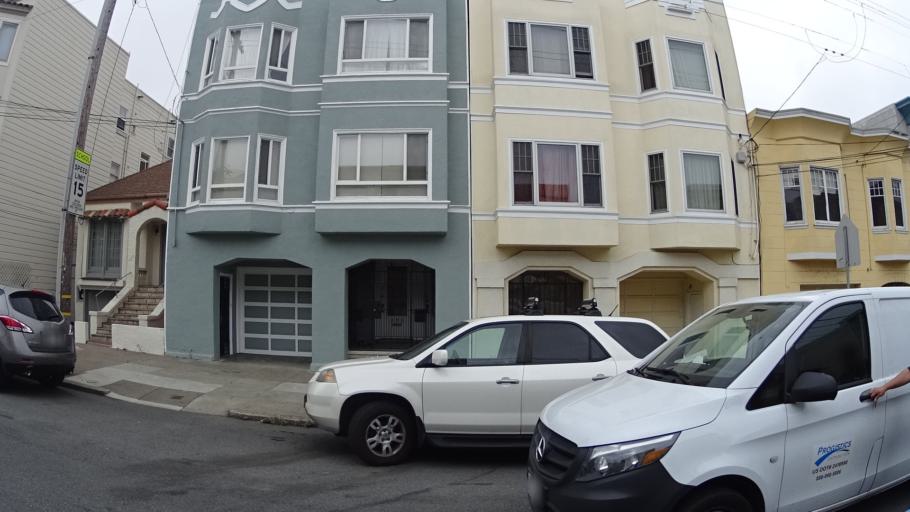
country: US
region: California
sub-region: San Francisco County
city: San Francisco
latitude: 37.7815
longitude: -122.4838
